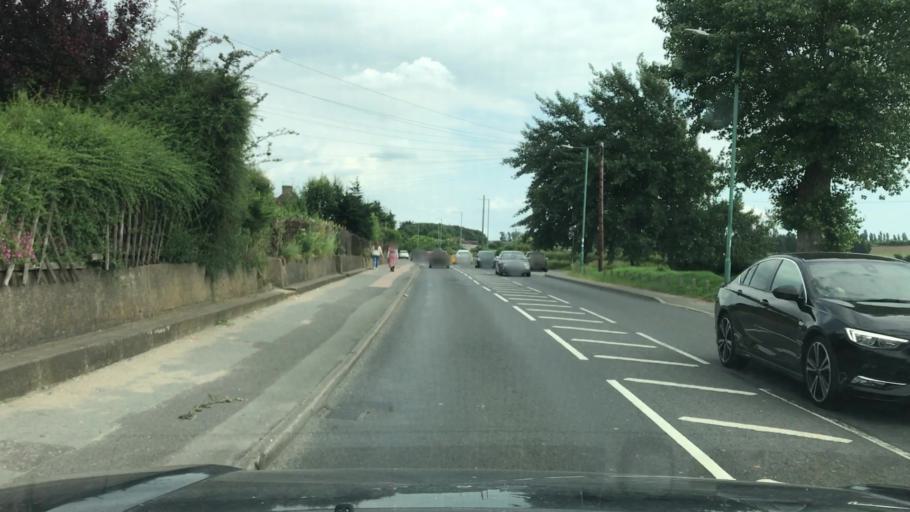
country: GB
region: England
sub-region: Kent
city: Stone
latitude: 51.4195
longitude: 0.2540
